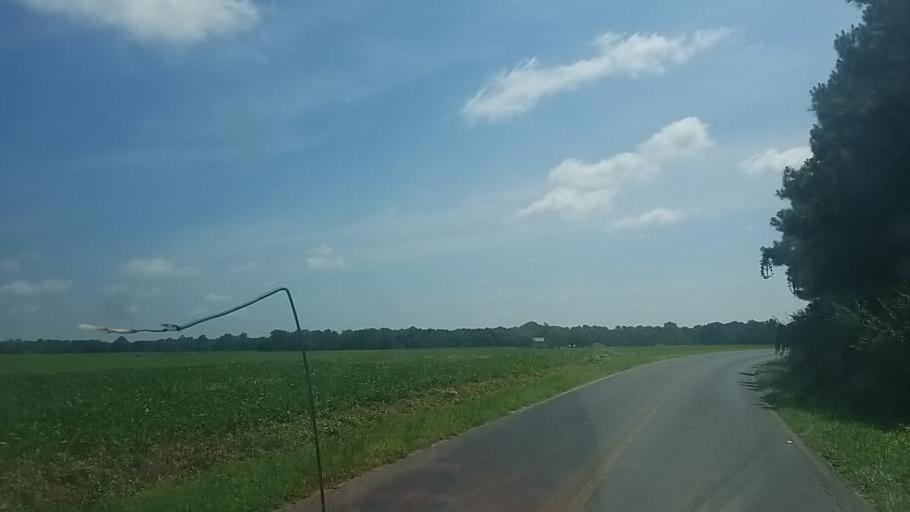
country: US
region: Maryland
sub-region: Caroline County
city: Ridgely
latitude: 38.8918
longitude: -75.9299
